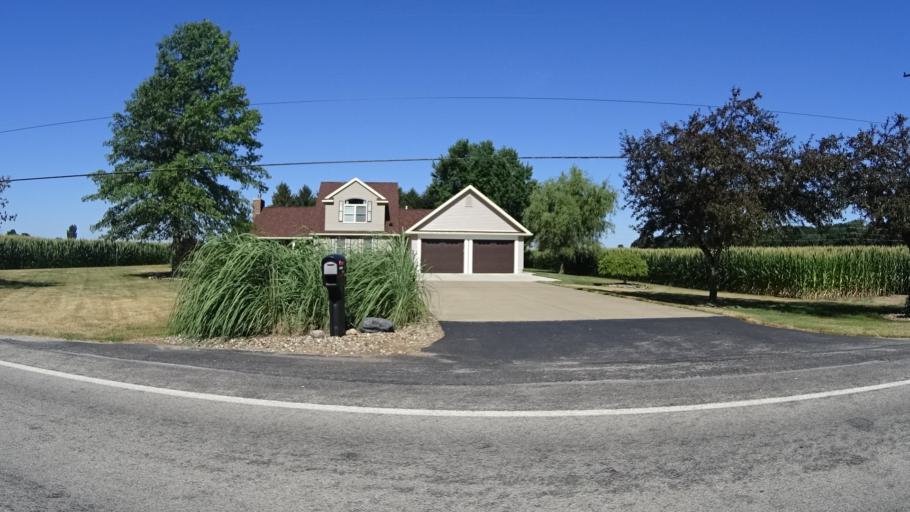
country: US
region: Ohio
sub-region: Erie County
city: Sandusky
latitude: 41.3665
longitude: -82.7277
